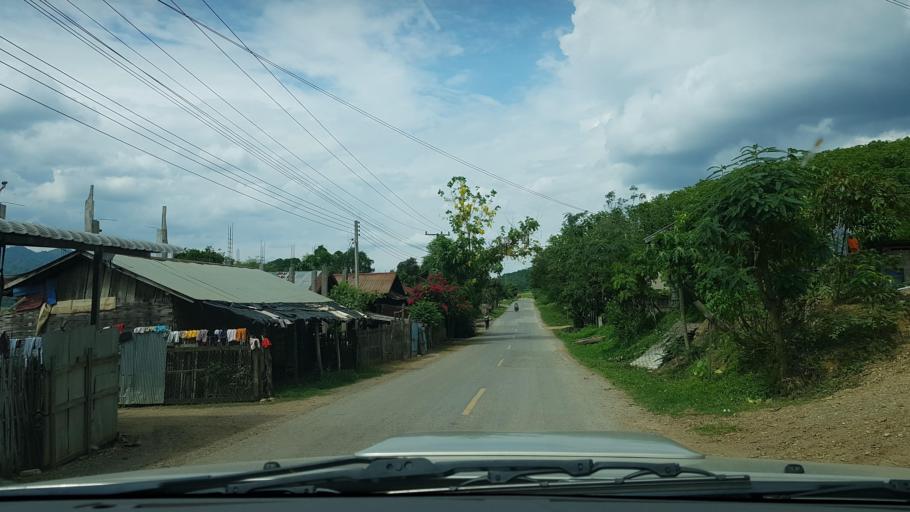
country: LA
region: Loungnamtha
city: Muang Nale
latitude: 20.2556
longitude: 101.5882
